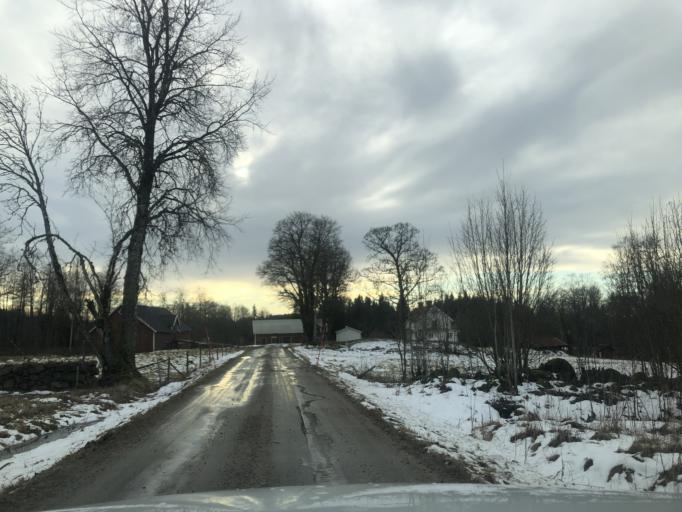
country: SE
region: Vaestra Goetaland
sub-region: Ulricehamns Kommun
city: Ulricehamn
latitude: 57.7942
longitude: 13.4874
